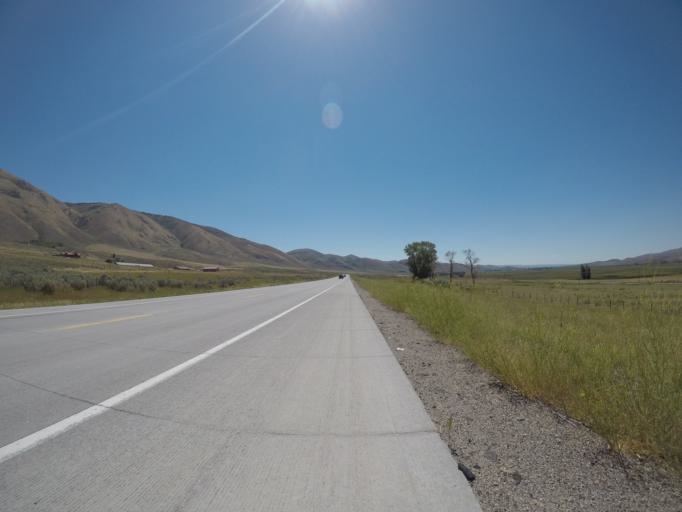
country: US
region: Idaho
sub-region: Bear Lake County
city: Montpelier
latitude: 42.1783
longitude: -111.0041
